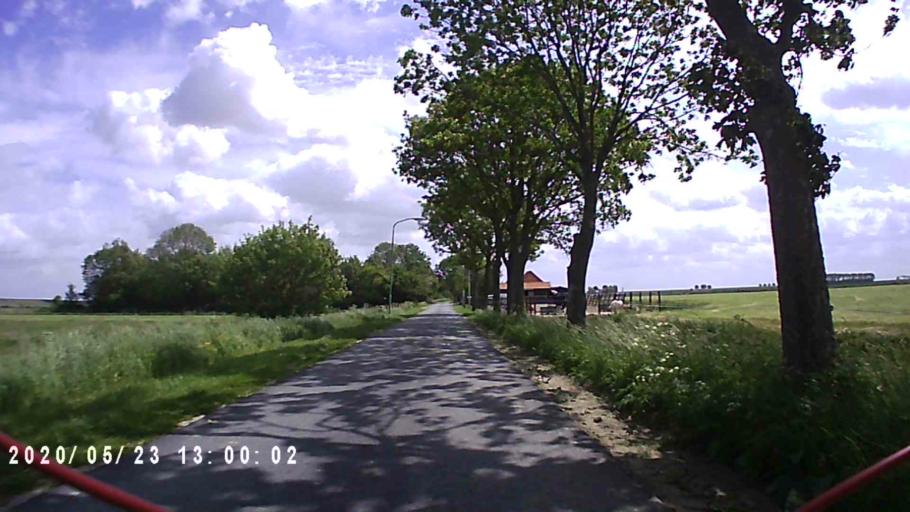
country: NL
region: Groningen
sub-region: Gemeente Delfzijl
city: Delfzijl
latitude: 53.2957
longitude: 7.0540
